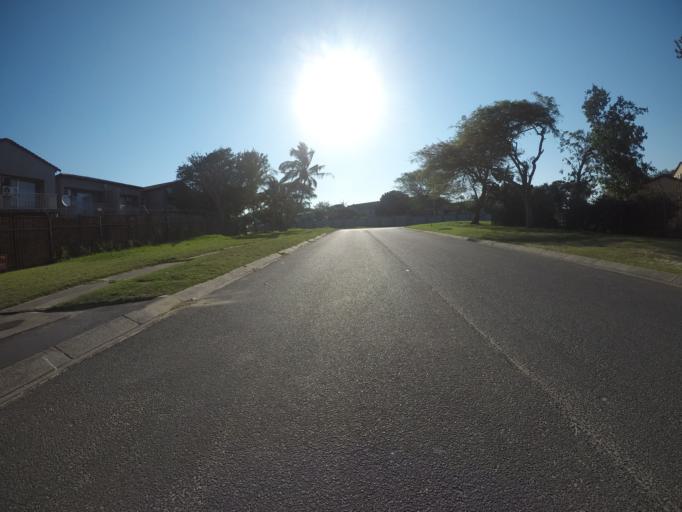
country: ZA
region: KwaZulu-Natal
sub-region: uThungulu District Municipality
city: Richards Bay
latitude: -28.7865
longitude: 32.1010
